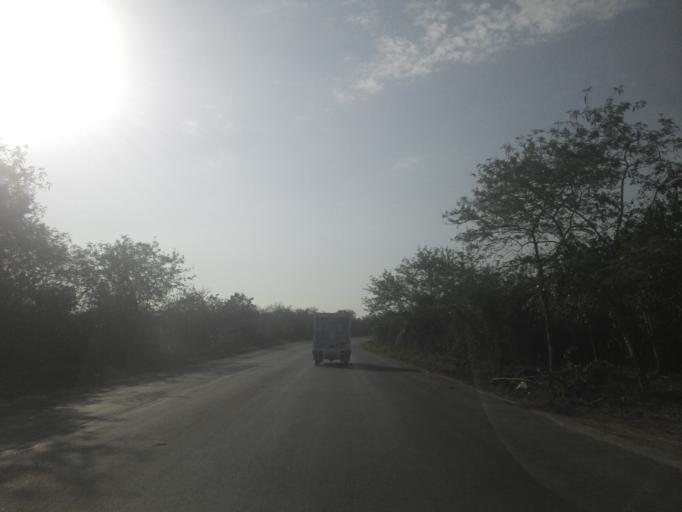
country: MX
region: Yucatan
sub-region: Valladolid
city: Tesoco
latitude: 20.7063
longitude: -88.1608
